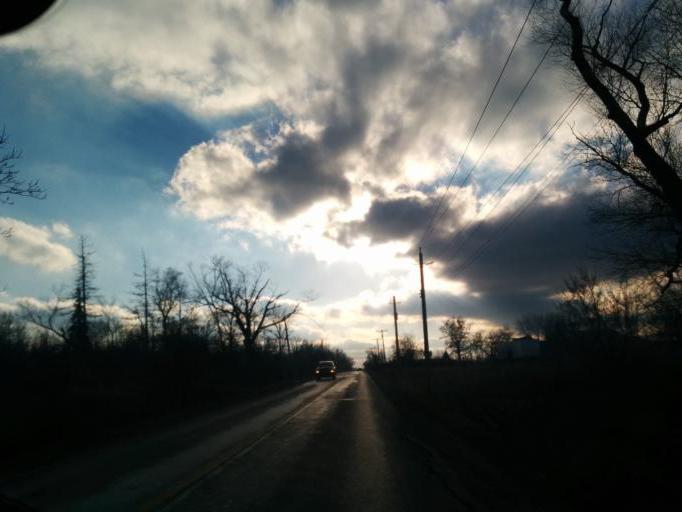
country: CA
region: Ontario
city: Oakville
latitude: 43.5124
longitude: -79.7265
